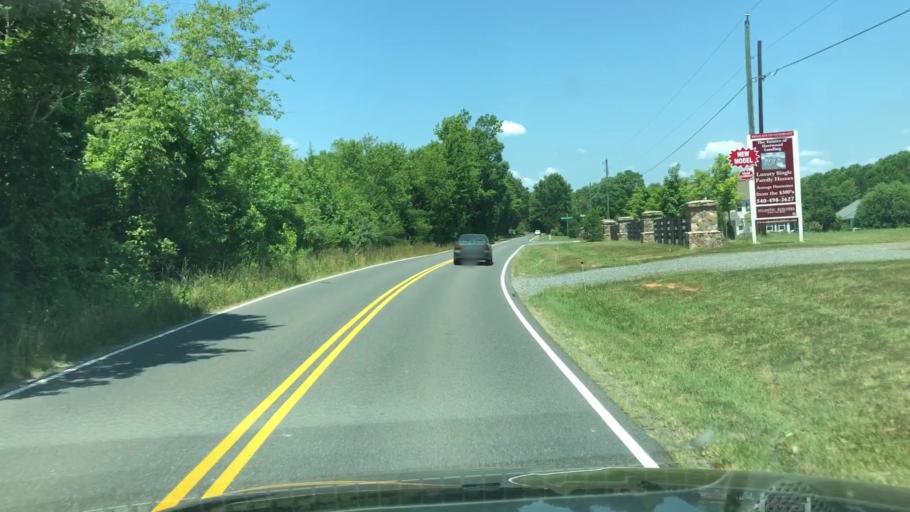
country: US
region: Virginia
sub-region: Stafford County
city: Falmouth
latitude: 38.4177
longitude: -77.5711
